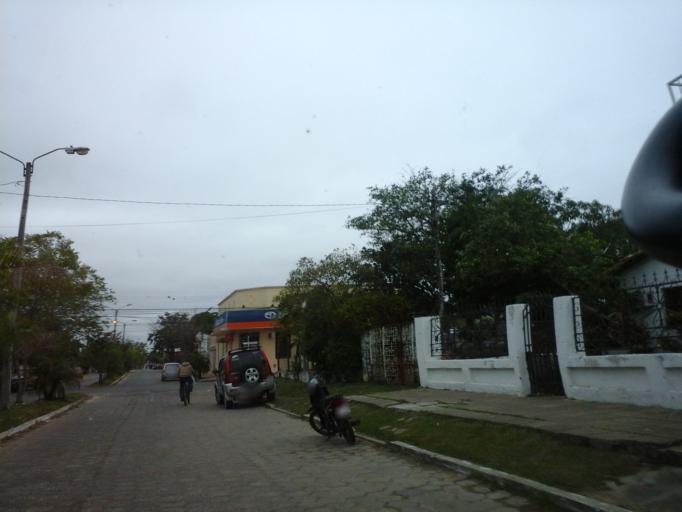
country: PY
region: Neembucu
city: Pilar
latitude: -26.8575
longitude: -58.2996
